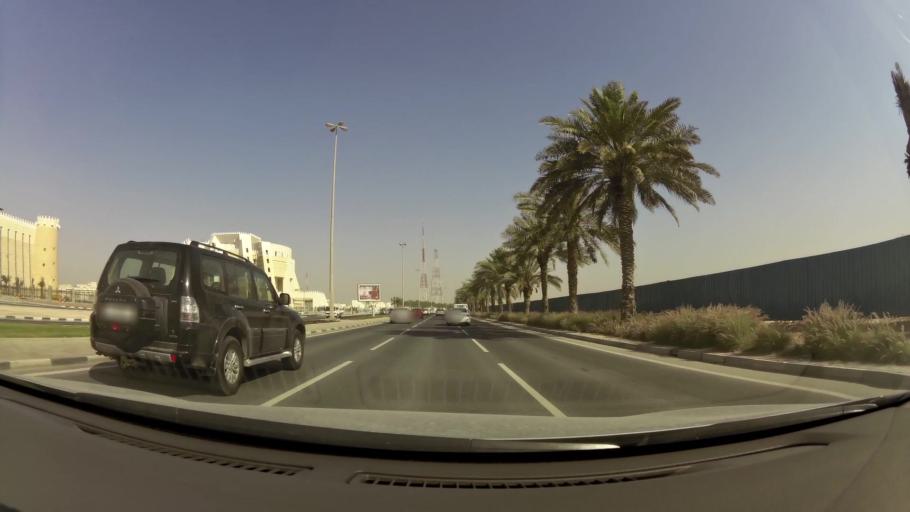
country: QA
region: Baladiyat ad Dawhah
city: Doha
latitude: 25.3058
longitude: 51.5058
